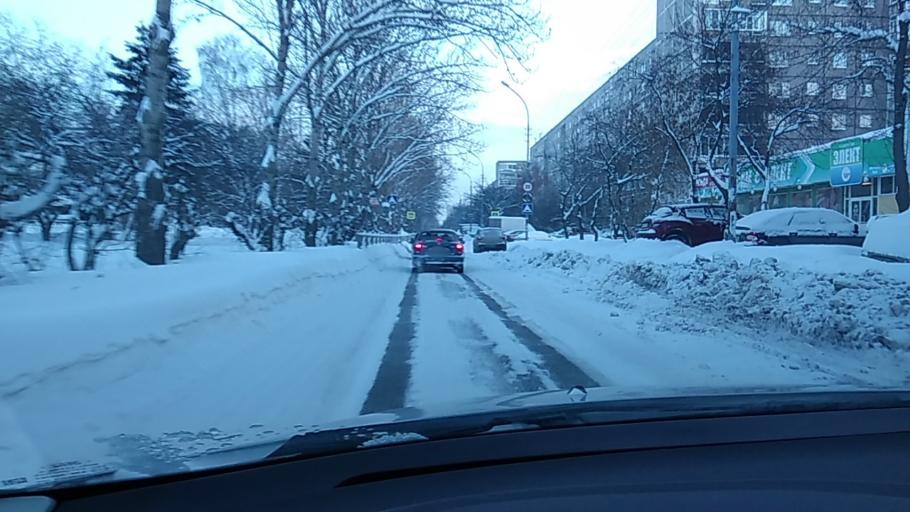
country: RU
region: Sverdlovsk
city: Sovkhoznyy
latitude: 56.8040
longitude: 60.5787
